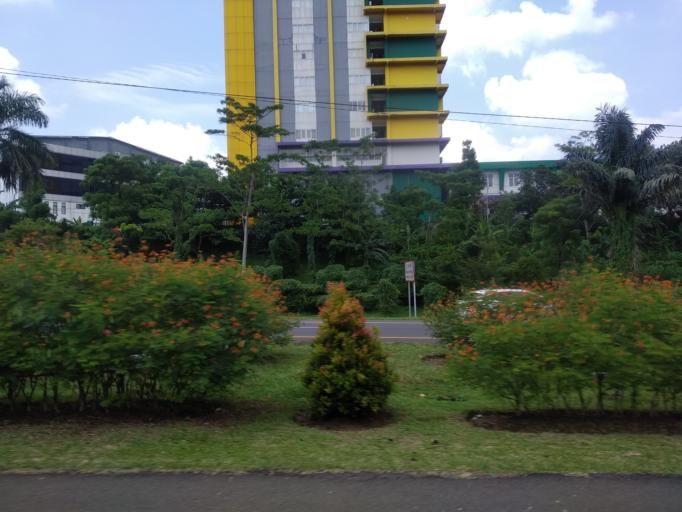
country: ID
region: West Java
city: Bogor
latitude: -6.6008
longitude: 106.8125
